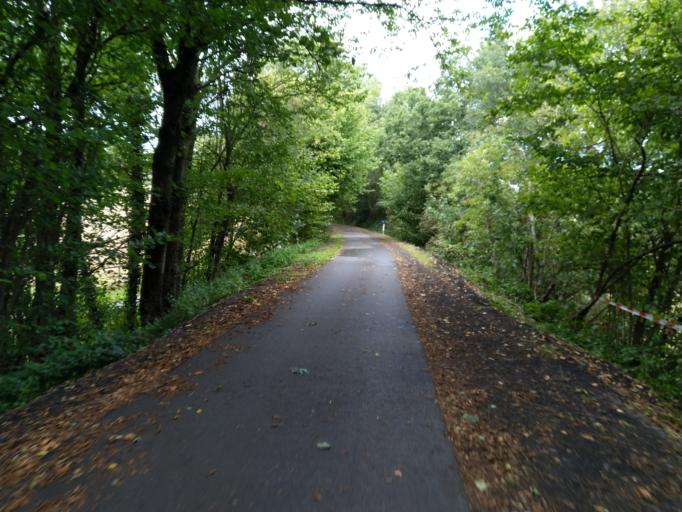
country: BE
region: Wallonia
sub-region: Province de Liege
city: Aubel
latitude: 50.6876
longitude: 5.8548
